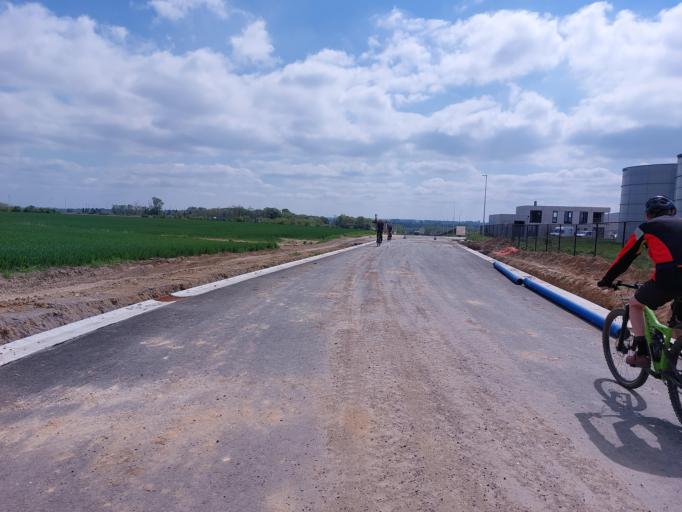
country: BE
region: Wallonia
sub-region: Province du Hainaut
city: Frameries
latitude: 50.4187
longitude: 3.9135
